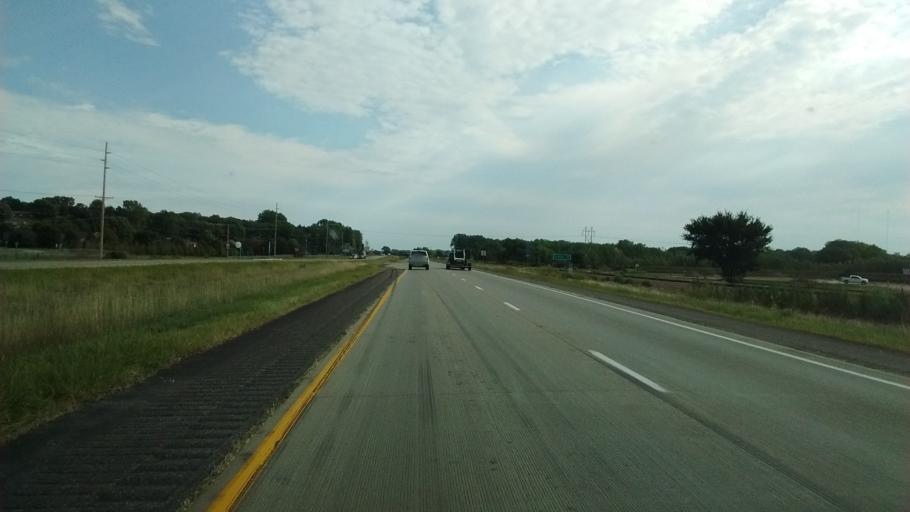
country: US
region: Iowa
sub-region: Woodbury County
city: Sioux City
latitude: 42.5631
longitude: -96.3298
